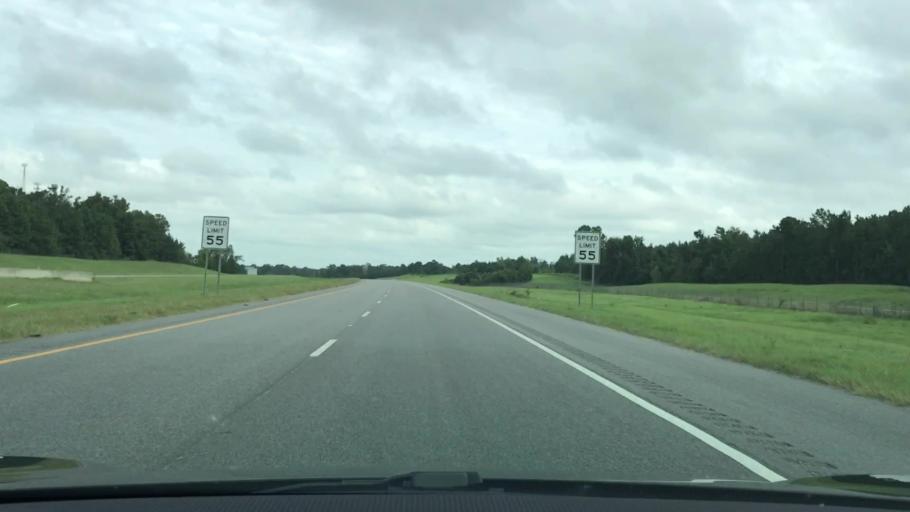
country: US
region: Alabama
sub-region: Montgomery County
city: Pike Road
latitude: 32.3450
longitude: -86.0640
